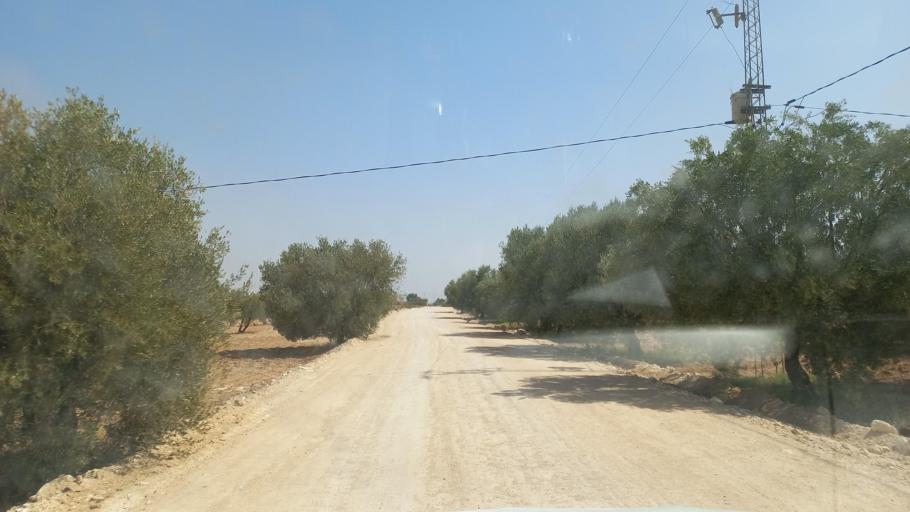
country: TN
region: Al Qasrayn
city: Kasserine
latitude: 35.2581
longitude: 9.0127
